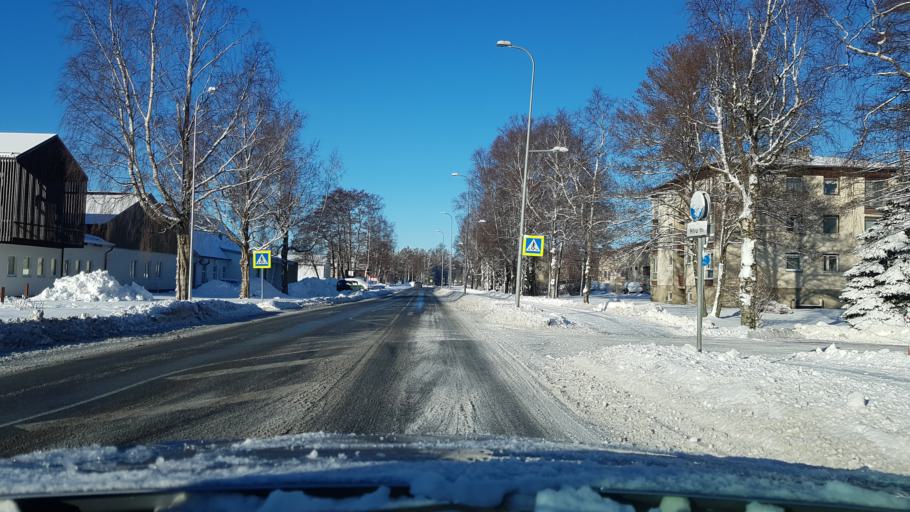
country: EE
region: Hiiumaa
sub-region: Kaerdla linn
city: Kardla
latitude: 58.9909
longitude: 22.7558
